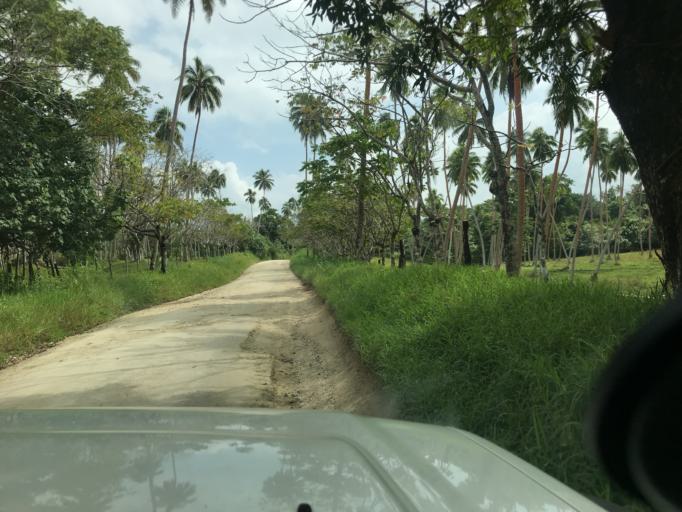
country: VU
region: Sanma
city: Luganville
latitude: -15.5826
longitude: 167.0438
